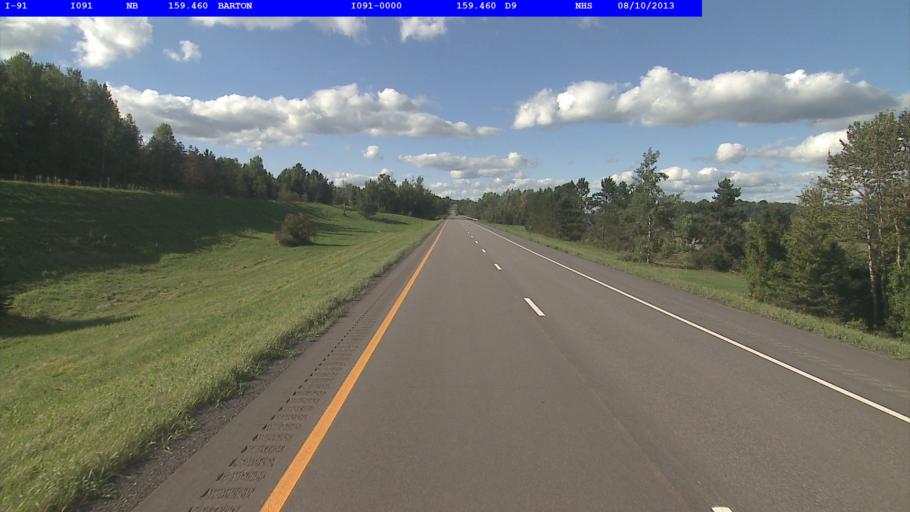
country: US
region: Vermont
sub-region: Orleans County
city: Newport
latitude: 44.7786
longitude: -72.2148
